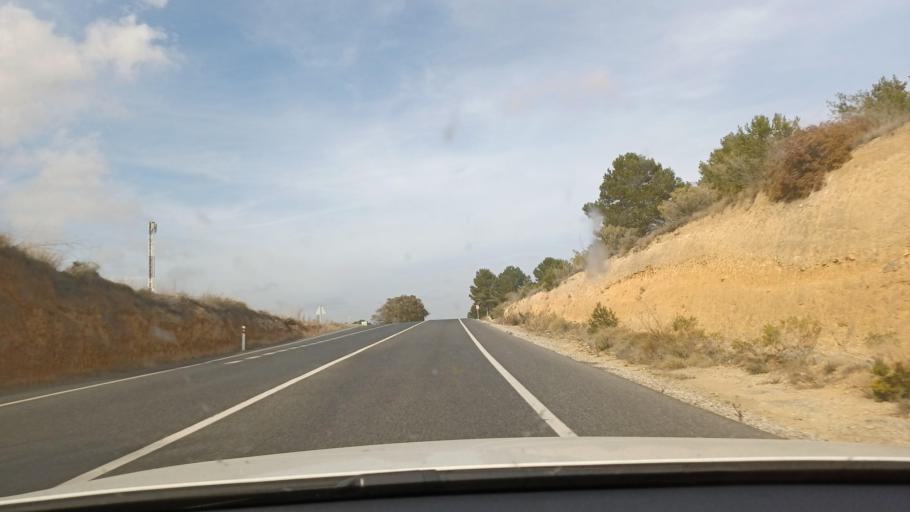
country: ES
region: Catalonia
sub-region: Provincia de Tarragona
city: la Pobla de Mafumet
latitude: 41.1715
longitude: 1.2396
